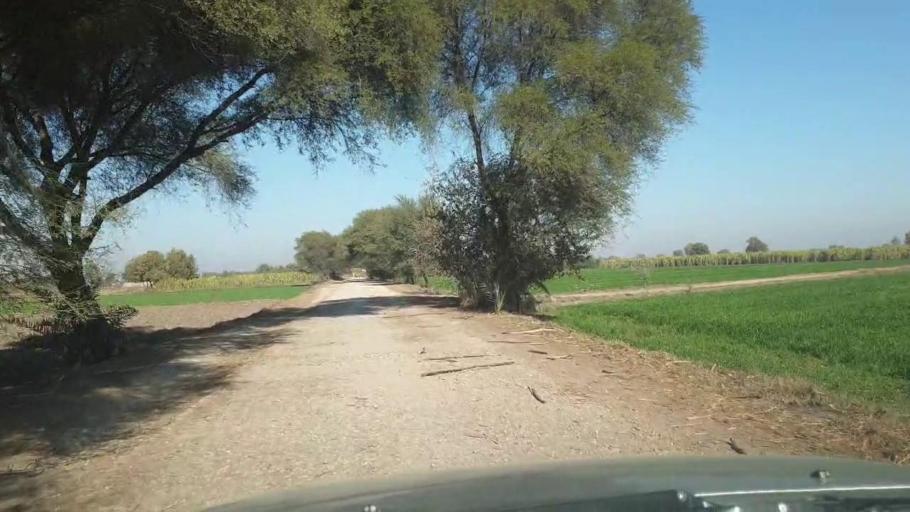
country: PK
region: Sindh
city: Ghotki
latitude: 28.0918
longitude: 69.3433
